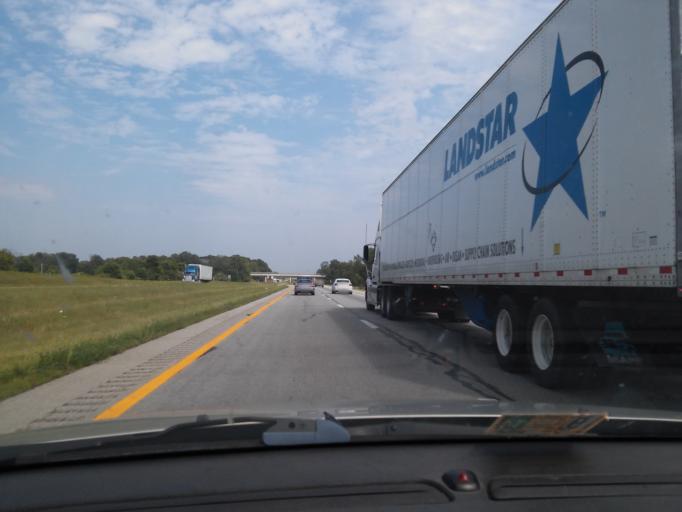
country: US
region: Ohio
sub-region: Montgomery County
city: Brookville
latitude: 39.8564
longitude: -84.3942
